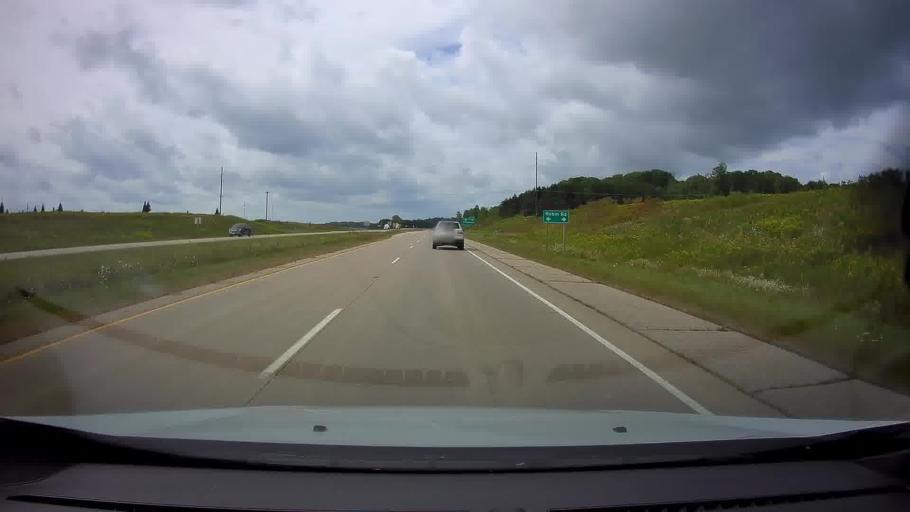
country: US
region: Wisconsin
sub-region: Shawano County
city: Wittenberg
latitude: 44.8229
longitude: -89.1411
